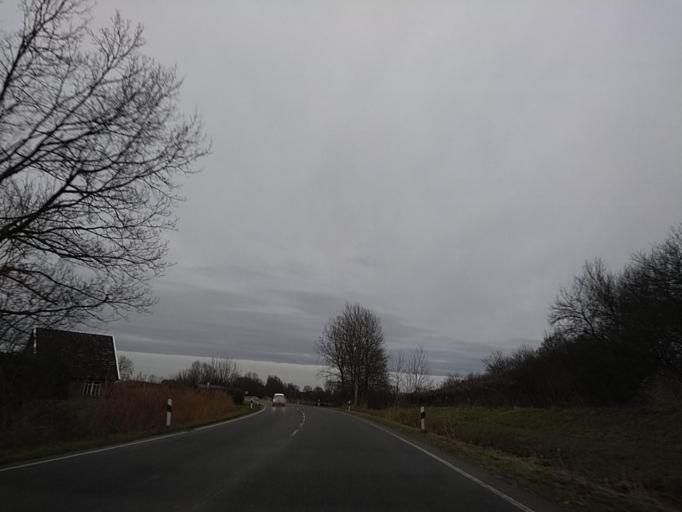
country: DE
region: Lower Saxony
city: Hinte
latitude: 53.3534
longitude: 7.0982
